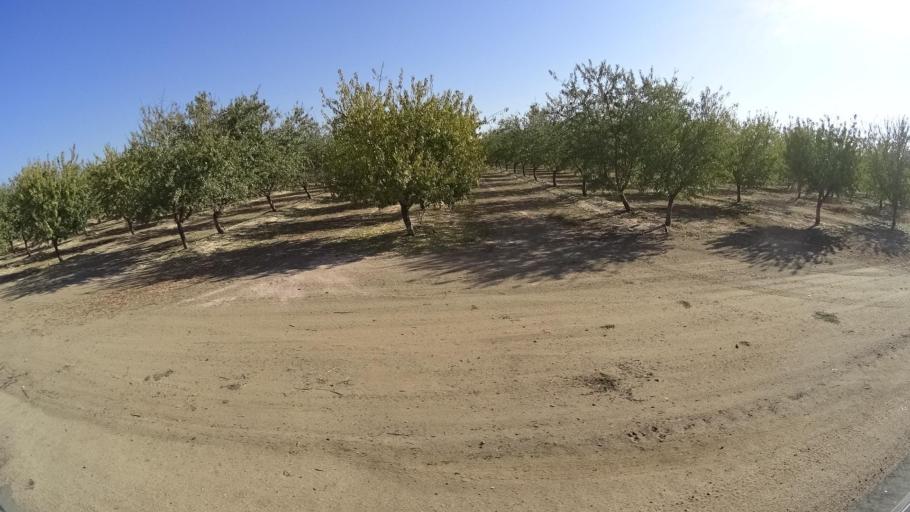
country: US
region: California
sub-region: Kern County
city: Delano
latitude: 35.7379
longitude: -119.2231
